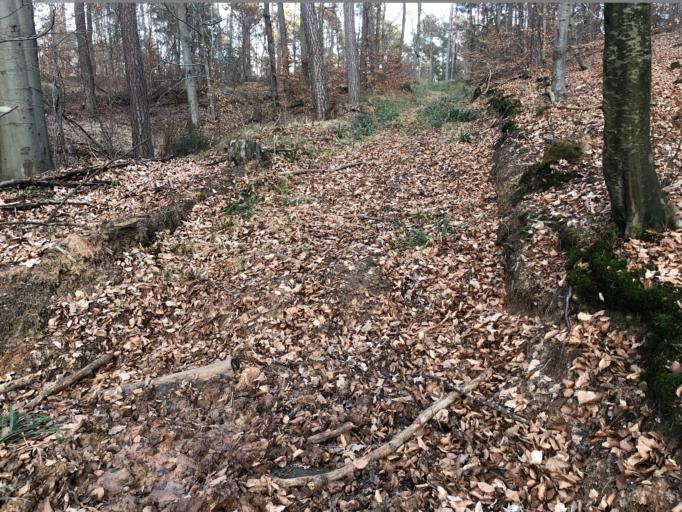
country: DE
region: Baden-Wuerttemberg
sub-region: Tuebingen Region
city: Tuebingen
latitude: 48.5108
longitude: 9.0120
